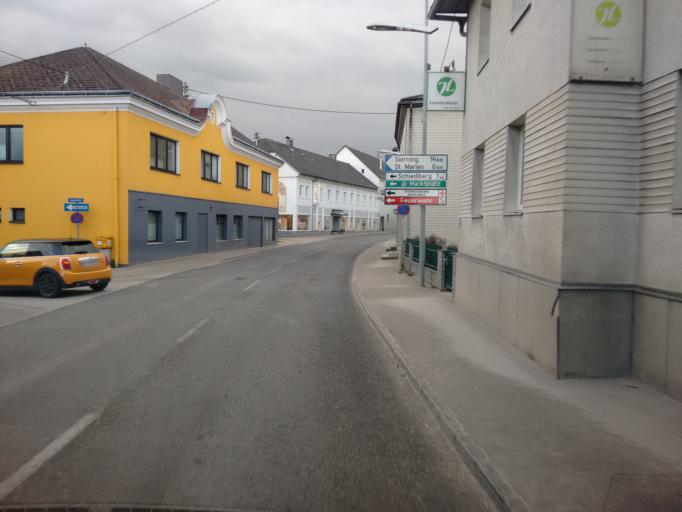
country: AT
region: Upper Austria
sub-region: Politischer Bezirk Linz-Land
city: Traun
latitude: 48.1391
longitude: 14.2283
